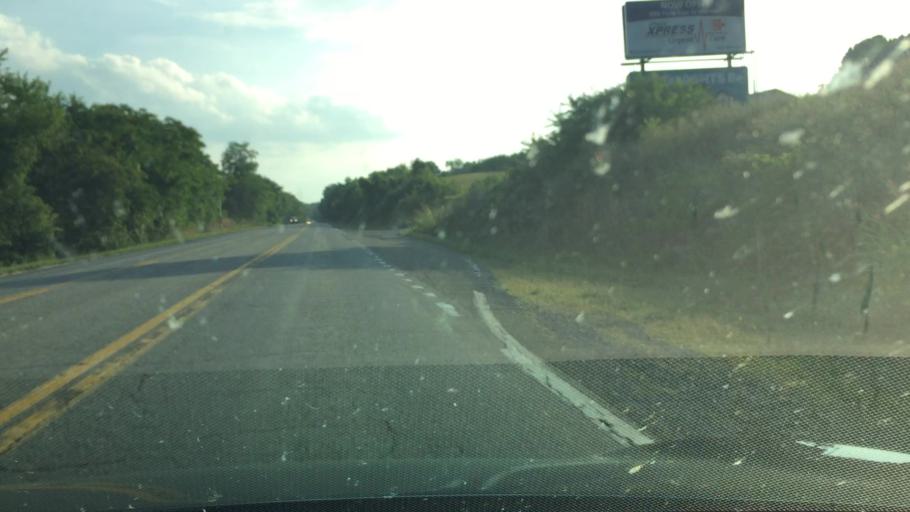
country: US
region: Virginia
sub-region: Pulaski County
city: Dublin
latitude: 37.1216
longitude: -80.6561
